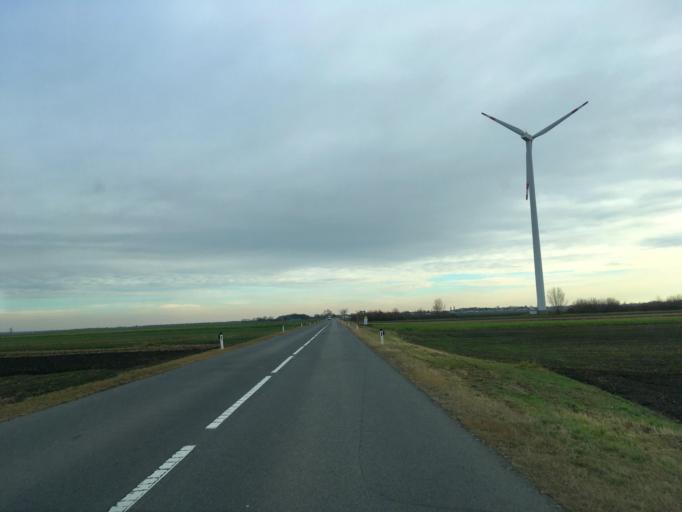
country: AT
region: Burgenland
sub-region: Politischer Bezirk Neusiedl am See
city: Pama
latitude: 48.0617
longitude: 17.0090
